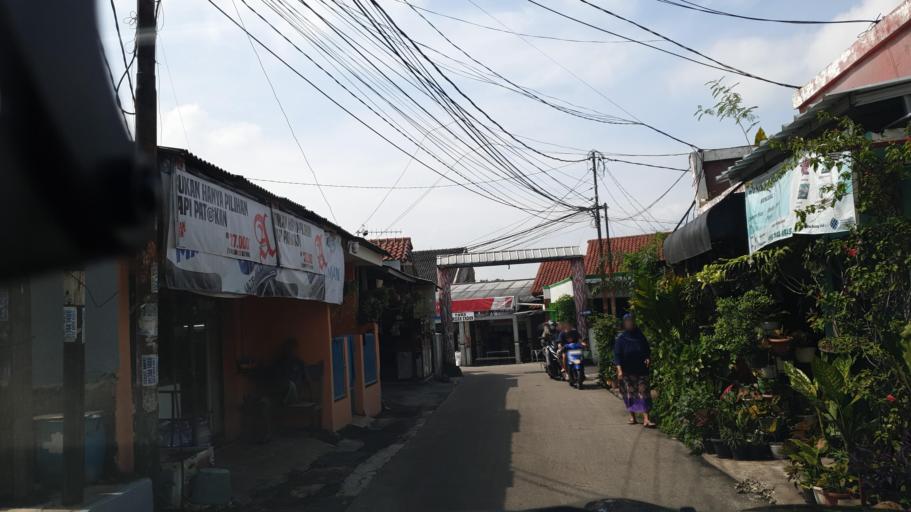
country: ID
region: West Java
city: Pamulang
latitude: -6.3259
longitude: 106.7594
